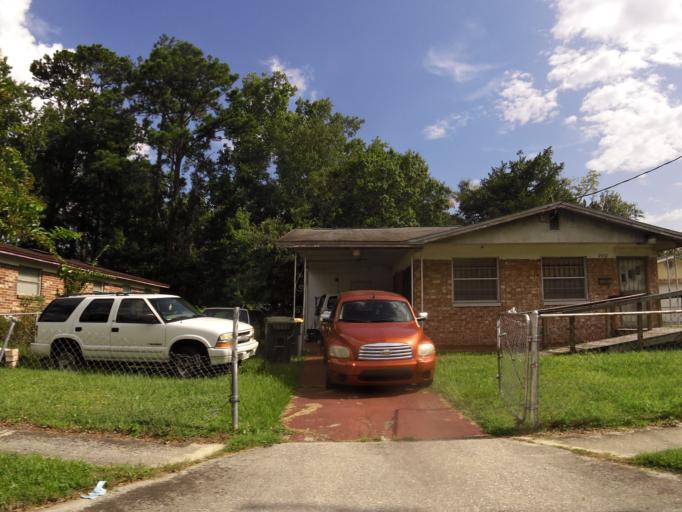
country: US
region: Florida
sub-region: Duval County
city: Jacksonville
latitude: 30.3647
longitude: -81.6893
